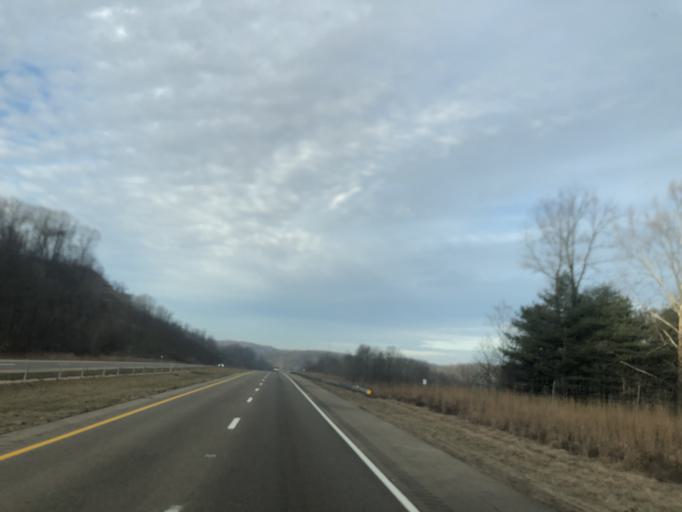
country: US
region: Ohio
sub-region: Athens County
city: Nelsonville
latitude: 39.4777
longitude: -82.3017
